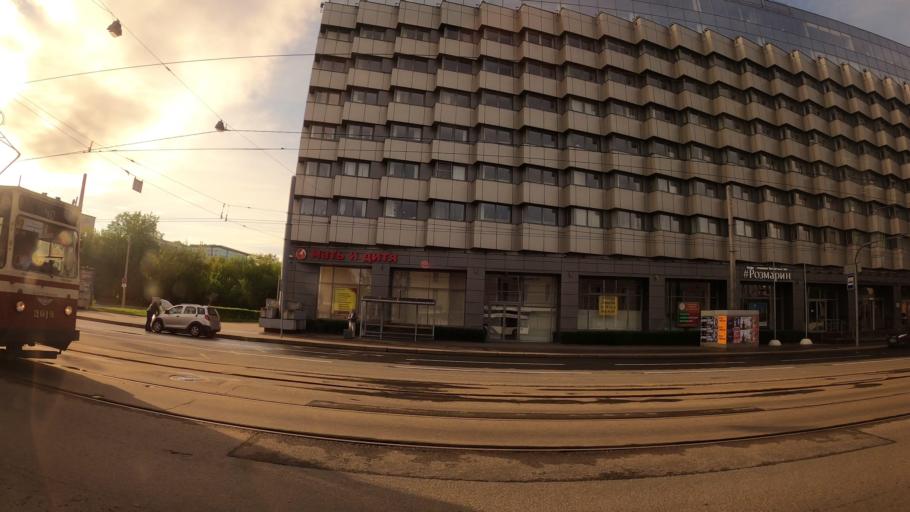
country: RU
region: St.-Petersburg
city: Vasyl'evsky Ostrov
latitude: 59.9344
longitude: 30.2486
